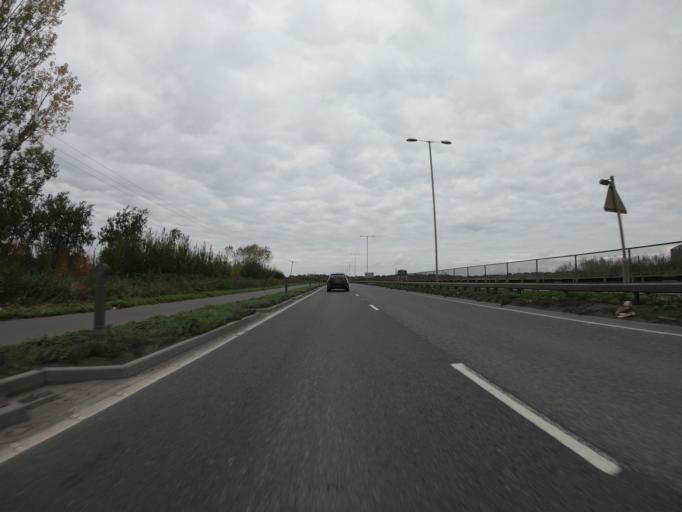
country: GB
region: England
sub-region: Borough of Thurrock
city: Tilbury
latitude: 51.4707
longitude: 0.3484
